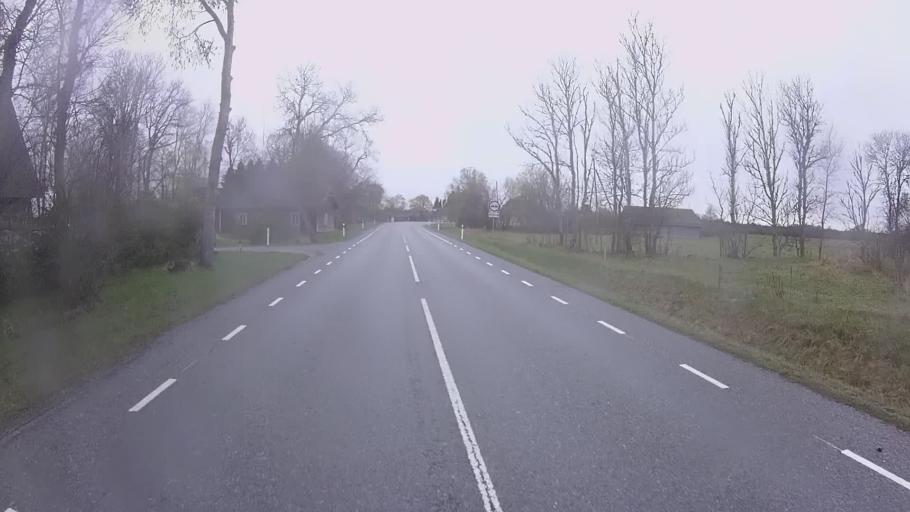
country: EE
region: Hiiumaa
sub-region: Kaerdla linn
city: Kardla
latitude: 58.9963
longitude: 22.5286
